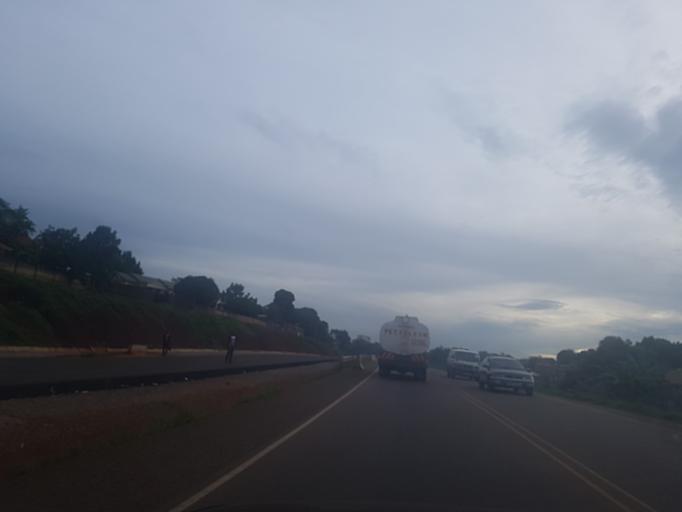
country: UG
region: Central Region
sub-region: Wakiso District
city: Kireka
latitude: 0.3679
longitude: 32.6138
